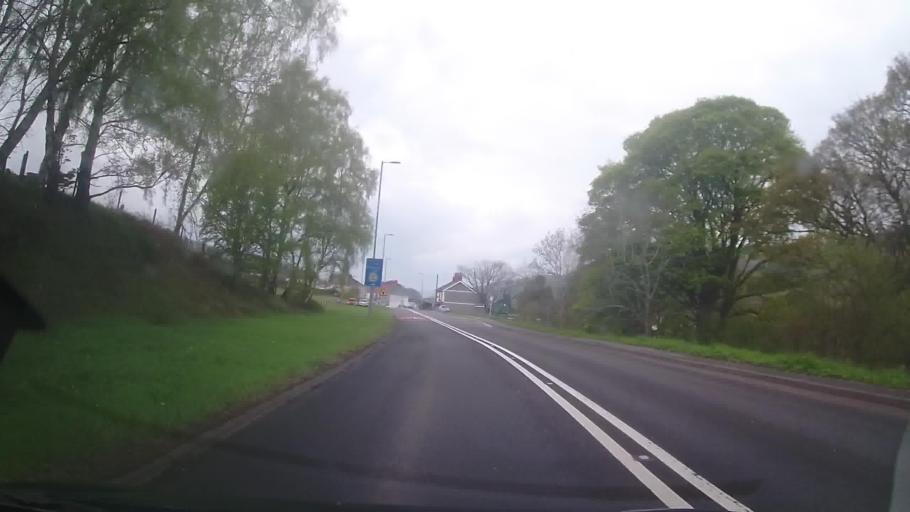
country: GB
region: Wales
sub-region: Denbighshire
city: Bryneglwys
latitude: 52.9790
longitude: -3.3105
